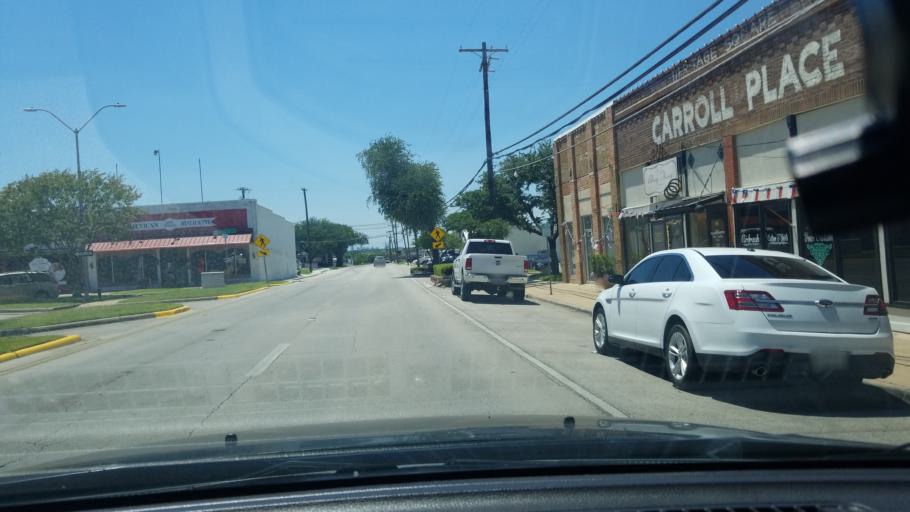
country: US
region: Texas
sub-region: Dallas County
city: Mesquite
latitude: 32.7670
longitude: -96.6007
